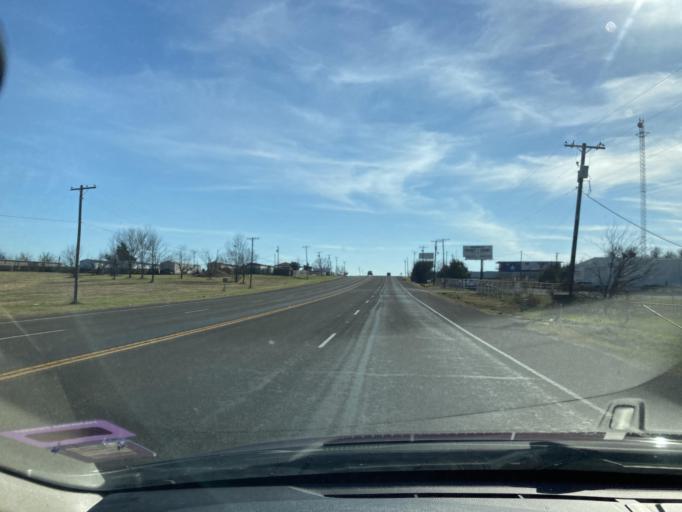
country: US
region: Texas
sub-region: Navarro County
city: Corsicana
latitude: 32.0814
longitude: -96.4530
